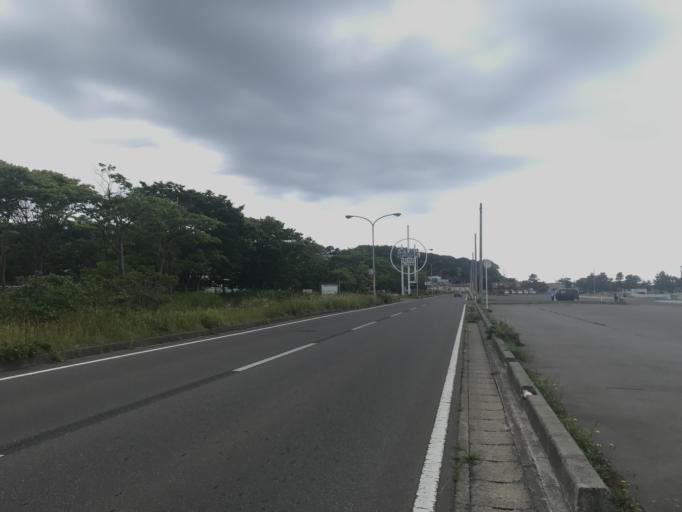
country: JP
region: Aomori
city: Shimokizukuri
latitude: 40.7791
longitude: 140.2126
